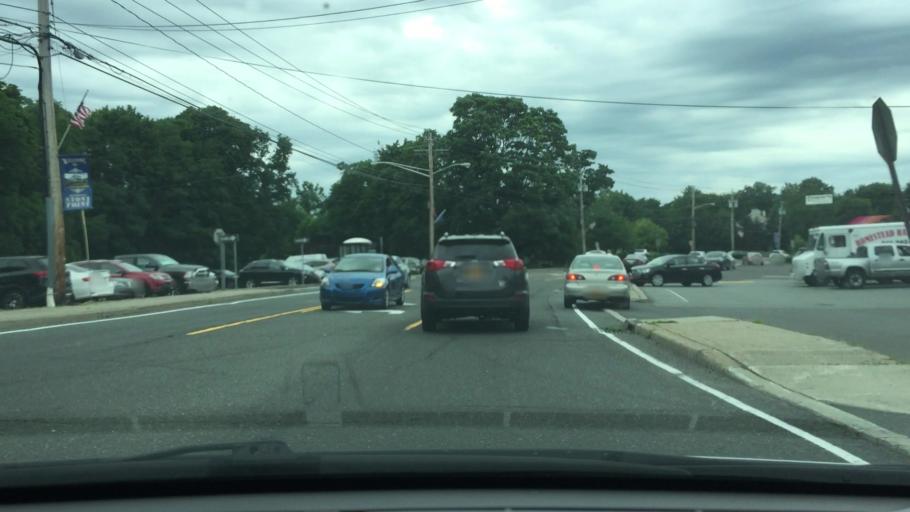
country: US
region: New York
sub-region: Rockland County
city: Stony Point
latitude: 41.2238
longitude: -73.9845
